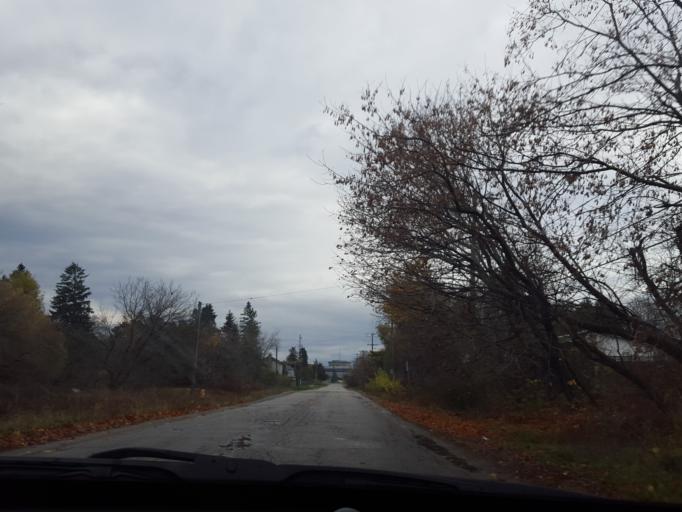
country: CA
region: Ontario
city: Ajax
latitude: 43.8233
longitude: -79.0741
